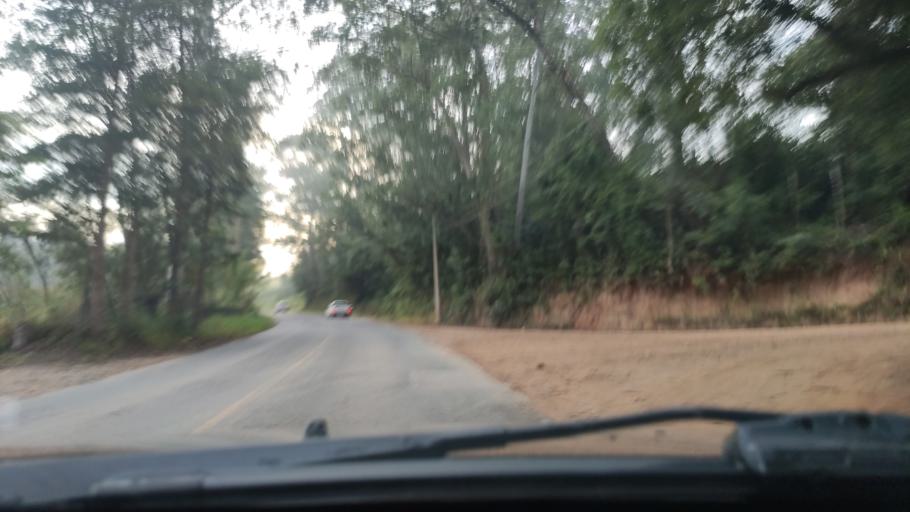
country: BR
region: Sao Paulo
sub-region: Campo Limpo Paulista
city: Campo Limpo Paulista
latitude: -23.1384
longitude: -46.7929
